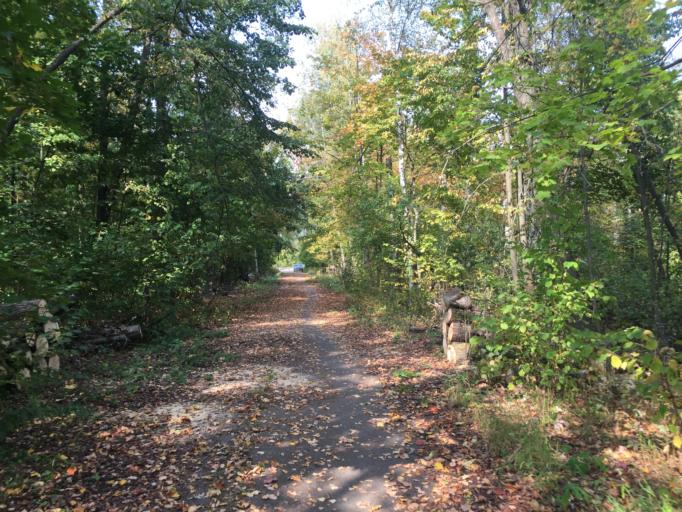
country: RU
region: Moscow
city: Babushkin
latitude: 55.8413
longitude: 37.7444
